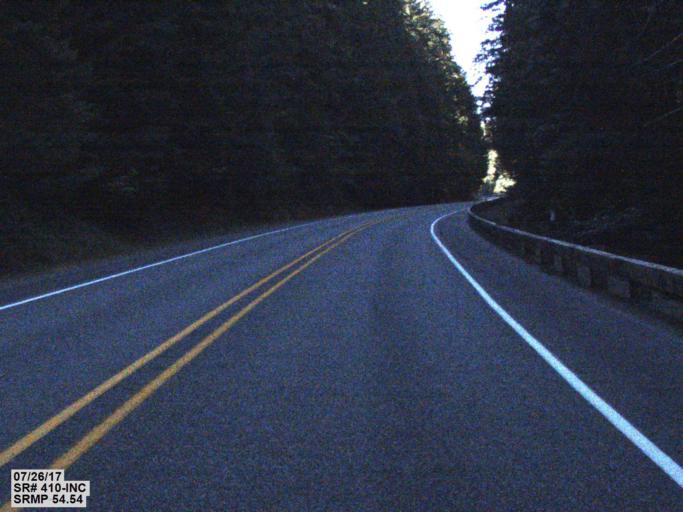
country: US
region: Washington
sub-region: King County
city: Enumclaw
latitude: 47.0211
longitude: -121.5326
